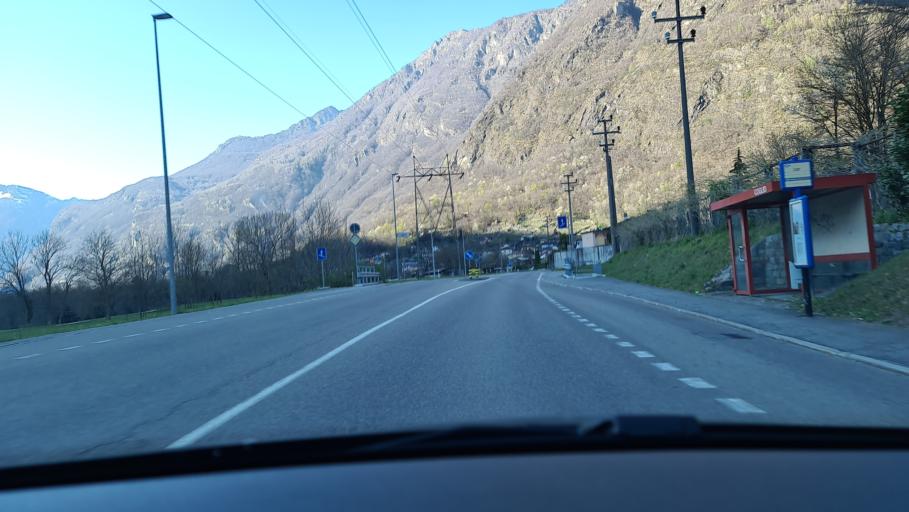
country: CH
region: Ticino
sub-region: Vallemaggia District
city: Cevio
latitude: 46.2686
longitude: 8.6832
